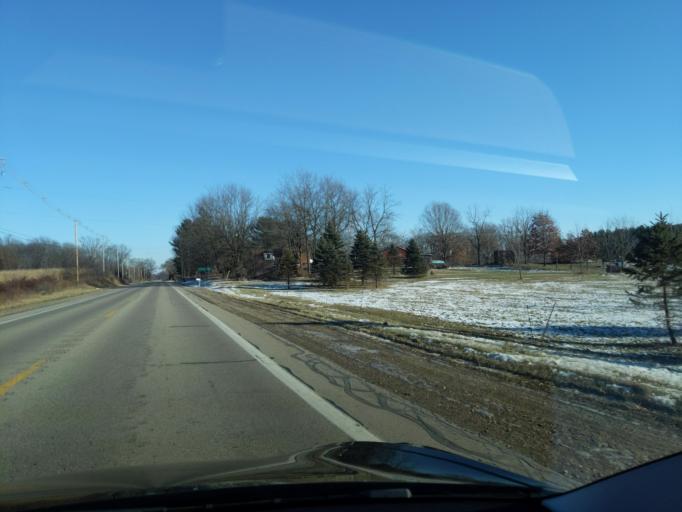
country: US
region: Michigan
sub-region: Ingham County
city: Stockbridge
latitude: 42.3937
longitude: -84.2741
